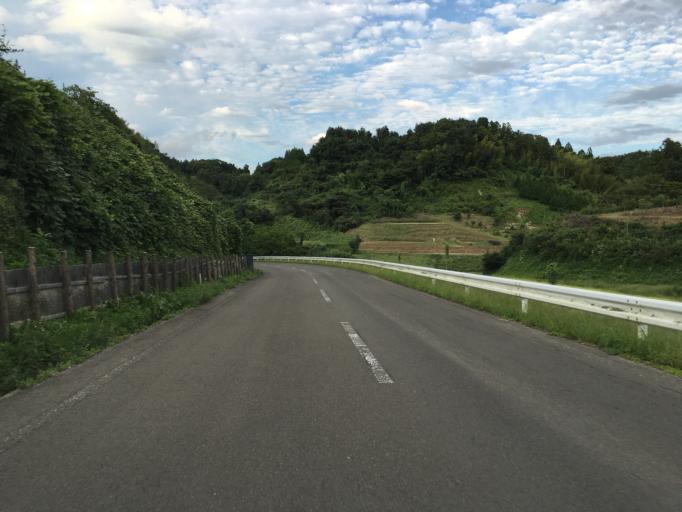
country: JP
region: Fukushima
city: Nihommatsu
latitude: 37.5969
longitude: 140.4969
